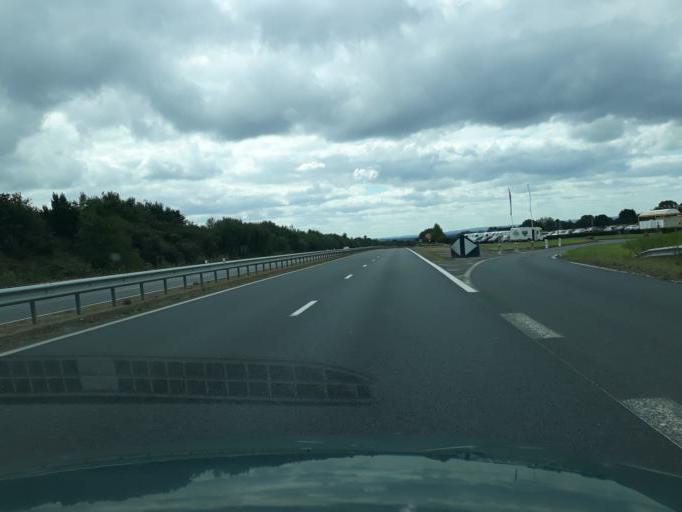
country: FR
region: Brittany
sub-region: Departement des Cotes-d'Armor
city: Plehedel
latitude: 48.7062
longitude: -3.0216
